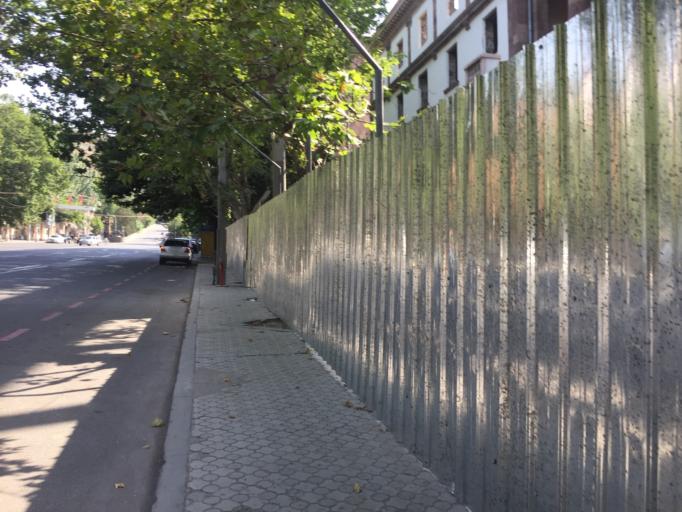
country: AM
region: Yerevan
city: Yerevan
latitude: 40.1897
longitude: 44.5183
